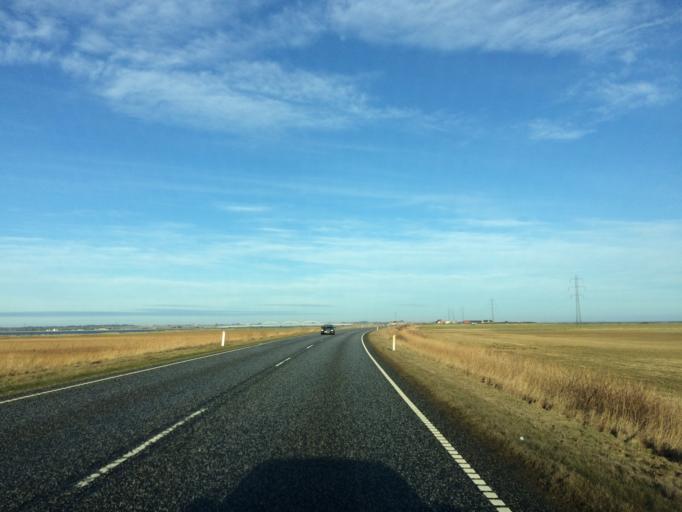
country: DK
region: Central Jutland
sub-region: Struer Kommune
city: Struer
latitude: 56.5610
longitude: 8.5574
